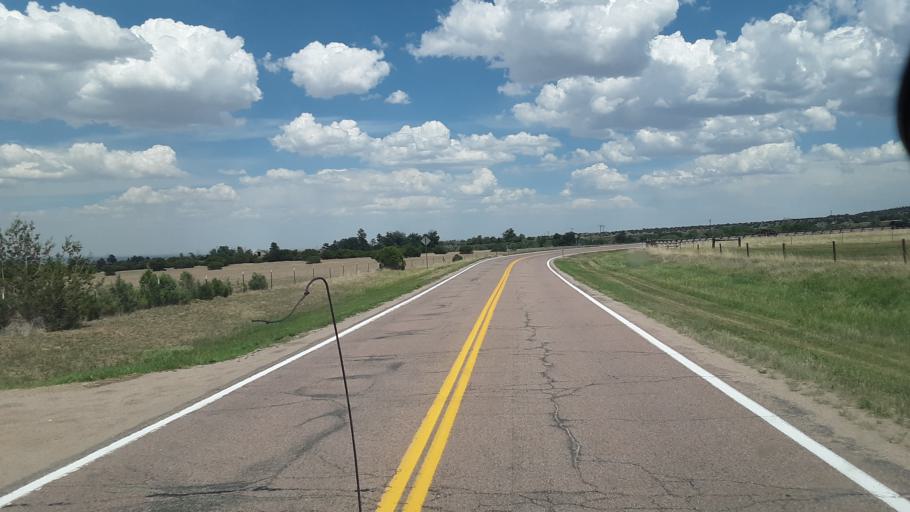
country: US
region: Colorado
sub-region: Fremont County
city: Florence
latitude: 38.2434
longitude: -105.0878
